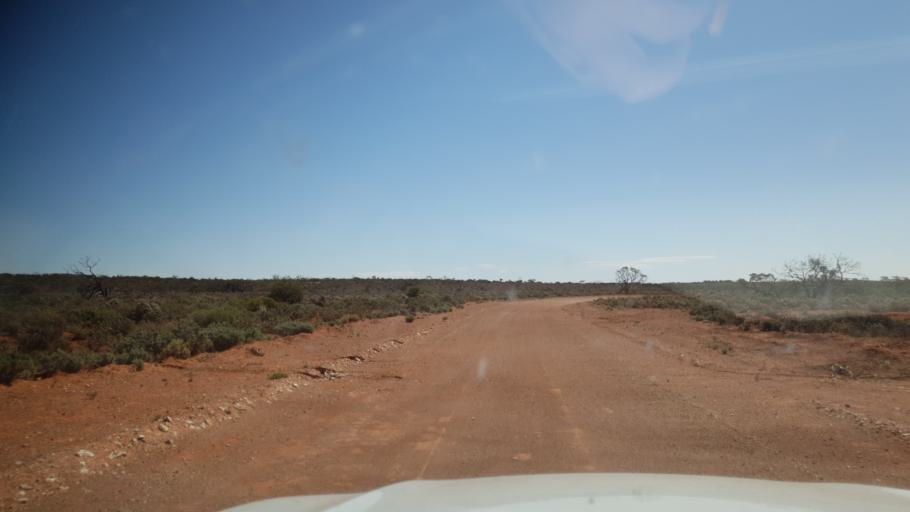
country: AU
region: South Australia
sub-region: Kimba
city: Caralue
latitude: -32.4875
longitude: 136.4432
